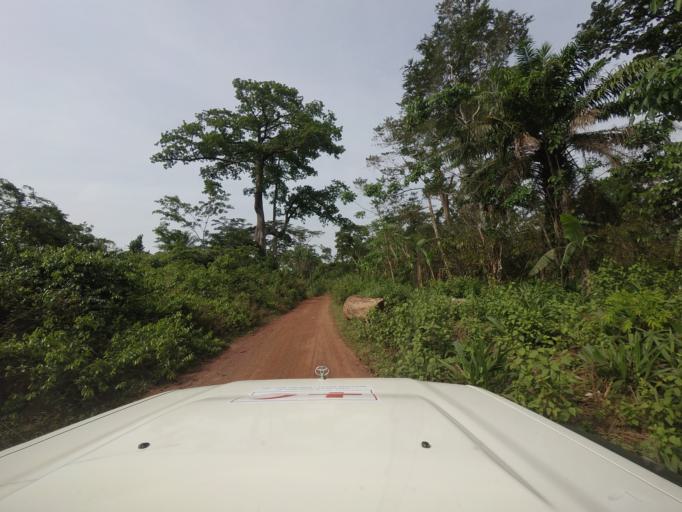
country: GN
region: Nzerekore
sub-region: Macenta
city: Macenta
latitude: 8.5000
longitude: -9.5324
